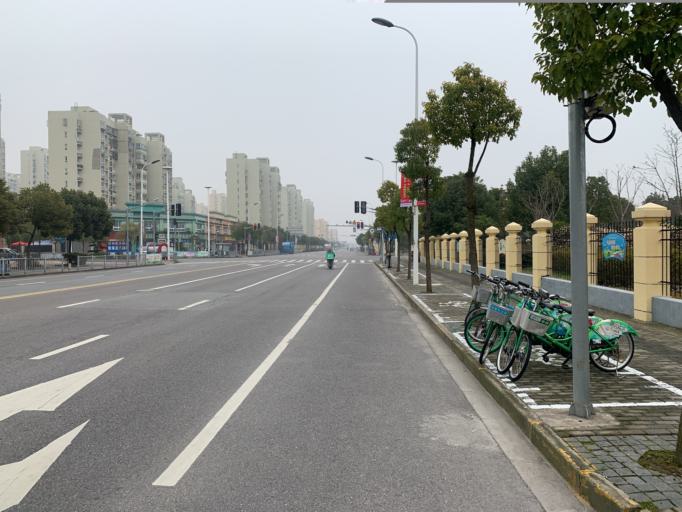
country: CN
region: Shanghai Shi
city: Huamu
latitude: 31.2412
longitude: 121.6241
